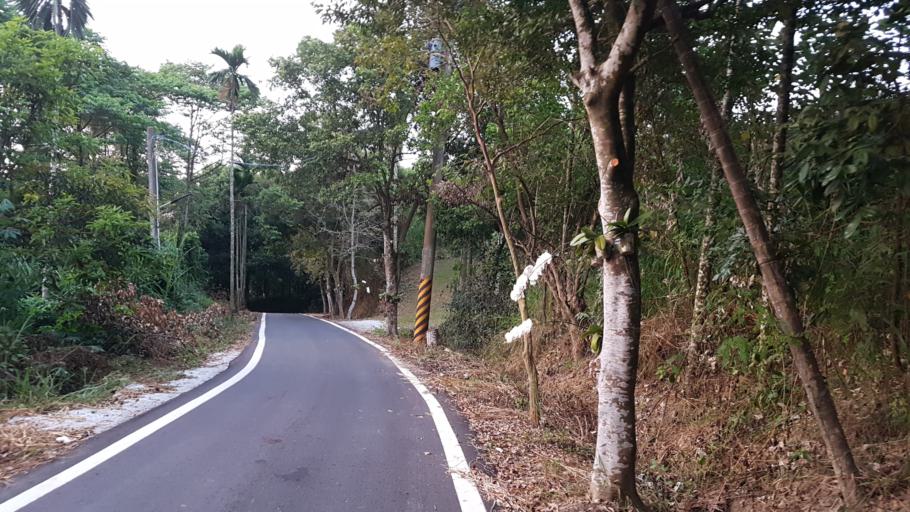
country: TW
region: Taiwan
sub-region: Chiayi
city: Jiayi Shi
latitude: 23.3628
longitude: 120.4659
